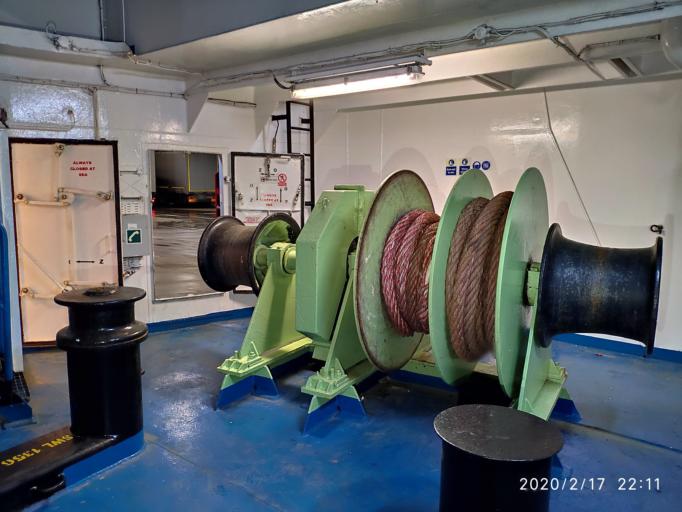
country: PL
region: West Pomeranian Voivodeship
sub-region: Swinoujscie
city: Swinoujscie
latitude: 53.8965
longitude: 14.2559
